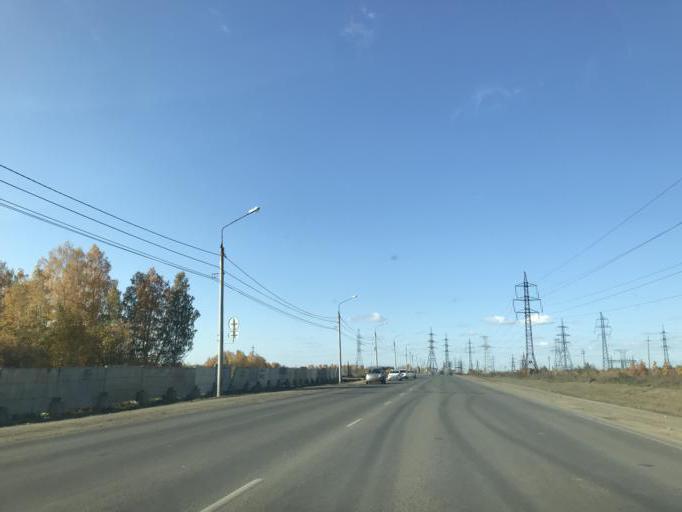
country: RU
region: Chelyabinsk
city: Roshchino
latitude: 55.2216
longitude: 61.2954
